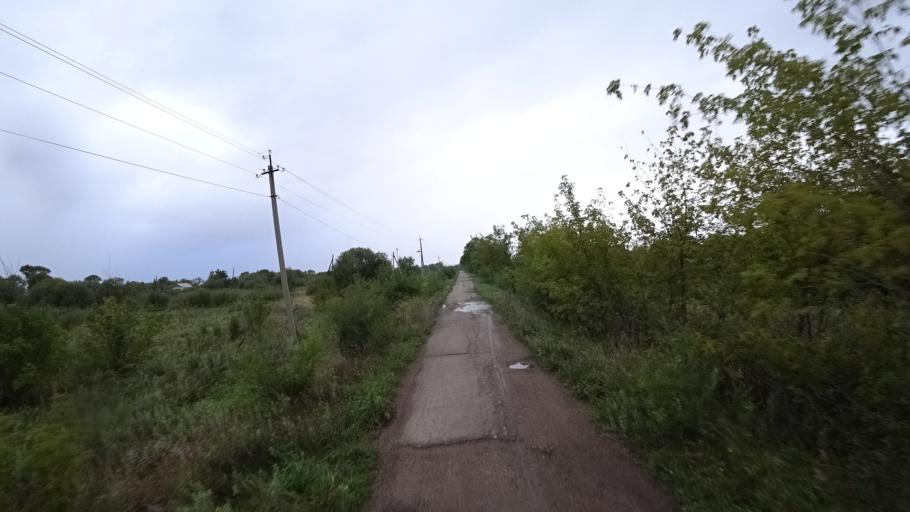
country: RU
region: Primorskiy
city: Chernigovka
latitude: 44.3990
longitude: 132.5313
